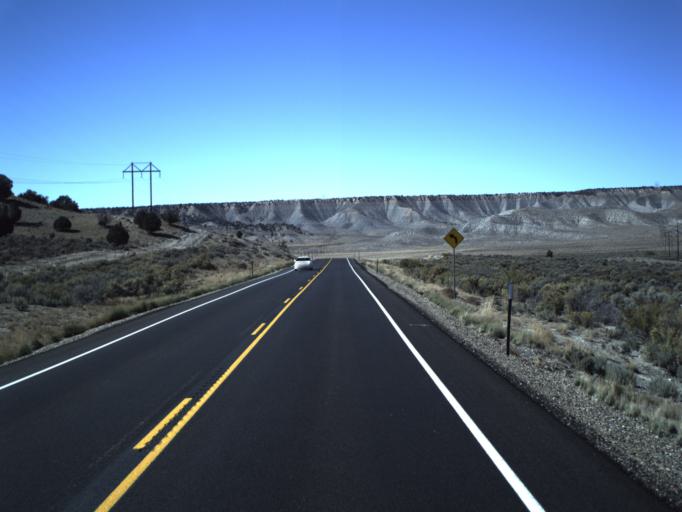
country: US
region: Utah
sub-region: Garfield County
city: Panguitch
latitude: 37.6010
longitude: -111.9578
